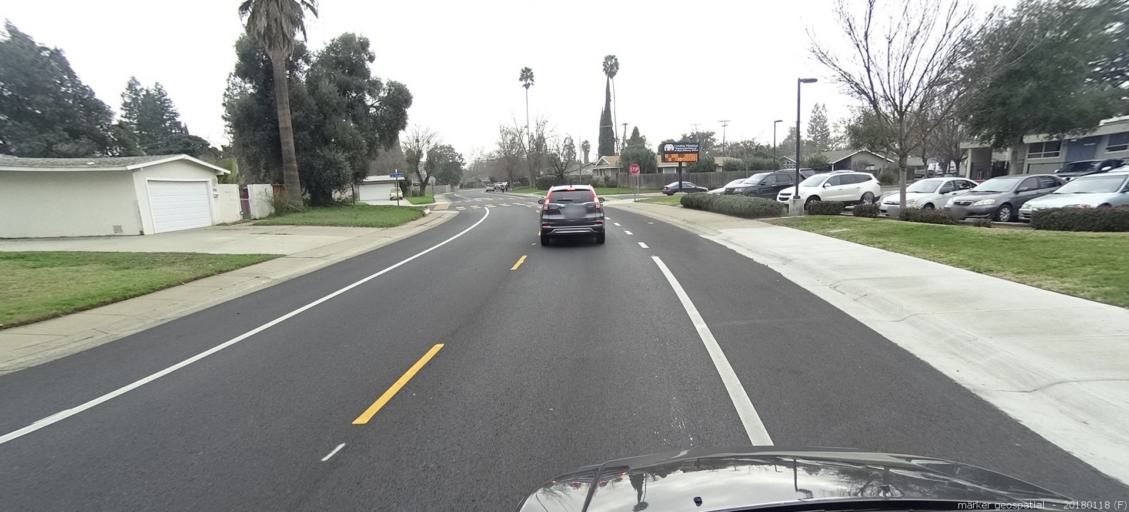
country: US
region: California
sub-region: Sacramento County
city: Rancho Cordova
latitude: 38.5898
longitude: -121.3155
